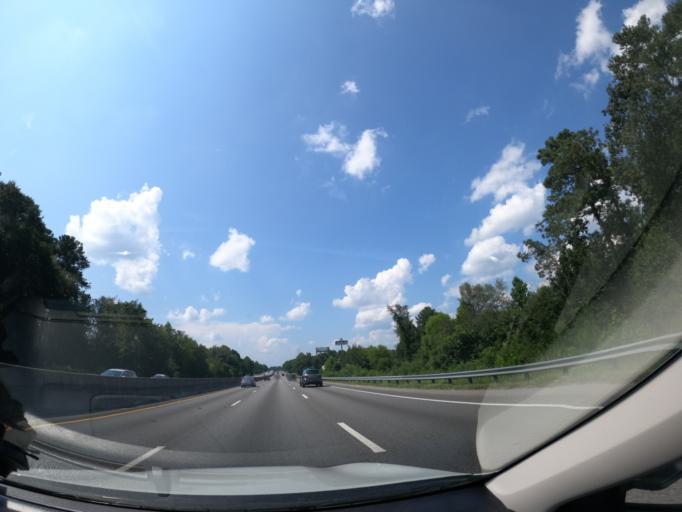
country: US
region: South Carolina
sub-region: Lexington County
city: Springdale
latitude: 33.9500
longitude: -81.0915
